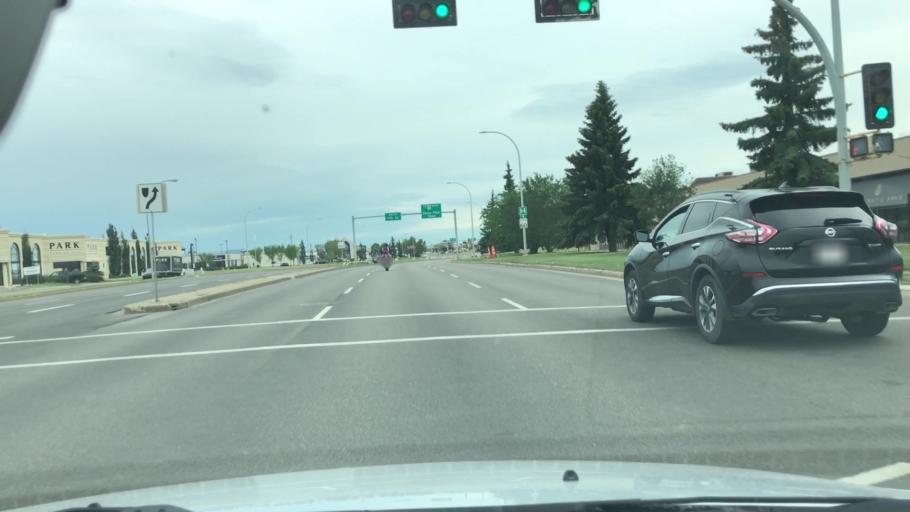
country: CA
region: Alberta
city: St. Albert
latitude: 53.5486
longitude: -113.6154
